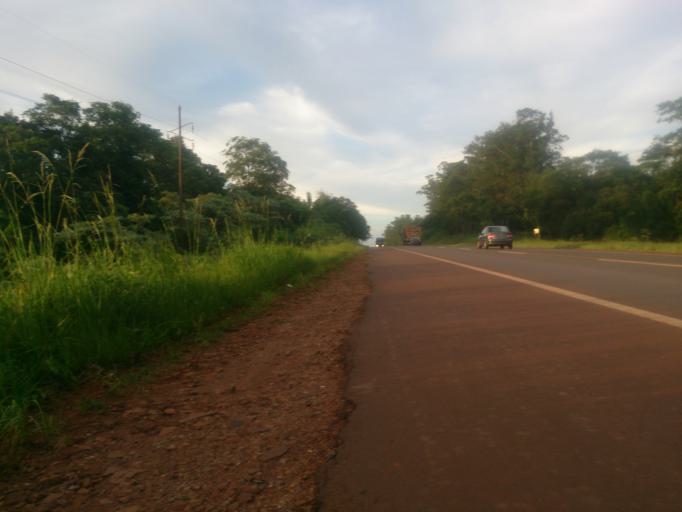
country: AR
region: Misiones
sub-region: Departamento de Obera
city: Obera
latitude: -27.4662
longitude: -55.0861
